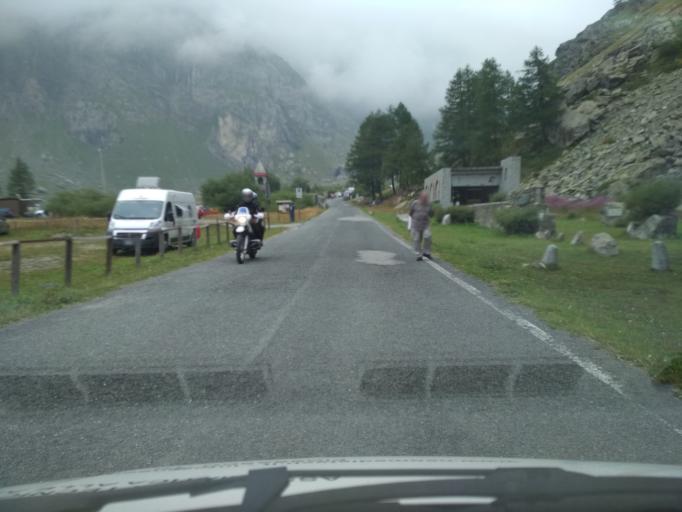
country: IT
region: Piedmont
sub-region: Provincia di Torino
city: Balme
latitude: 45.3056
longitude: 7.1689
